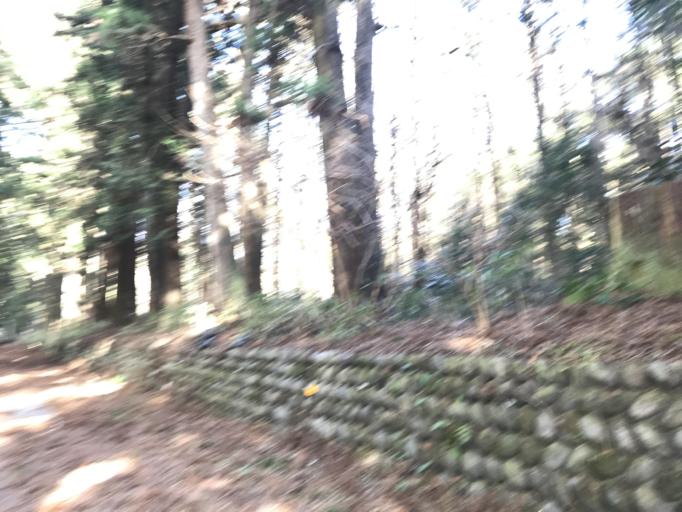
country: JP
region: Tochigi
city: Imaichi
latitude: 36.6768
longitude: 139.7211
